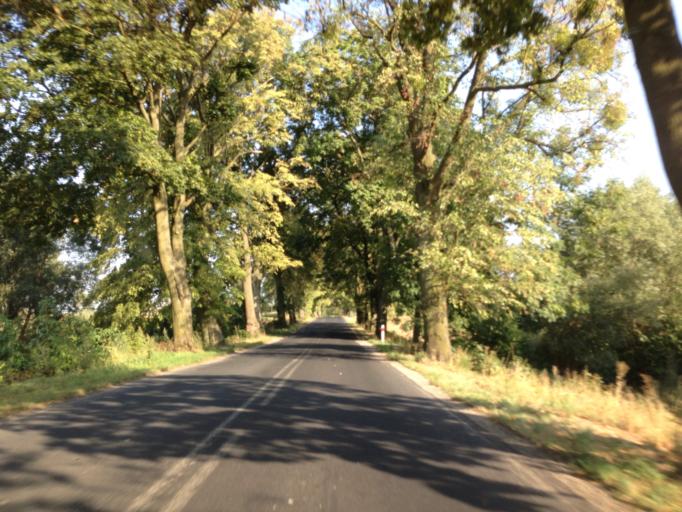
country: PL
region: Kujawsko-Pomorskie
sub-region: Powiat grudziadzki
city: Lasin
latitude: 53.5154
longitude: 19.1562
